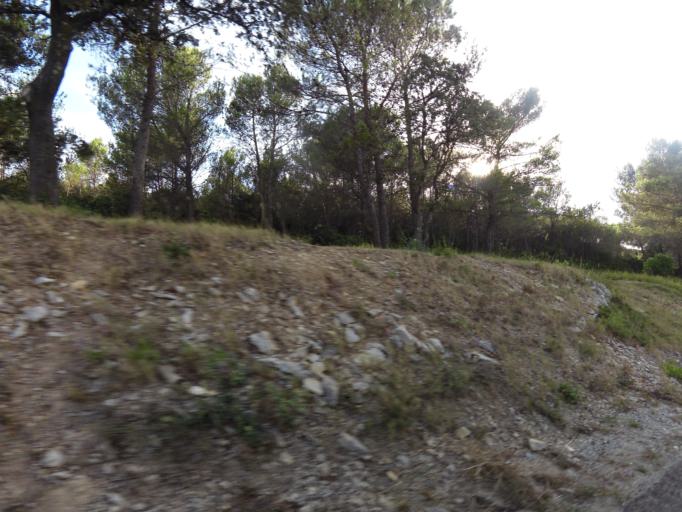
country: FR
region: Languedoc-Roussillon
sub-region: Departement du Gard
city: Congenies
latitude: 43.7924
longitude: 4.1649
